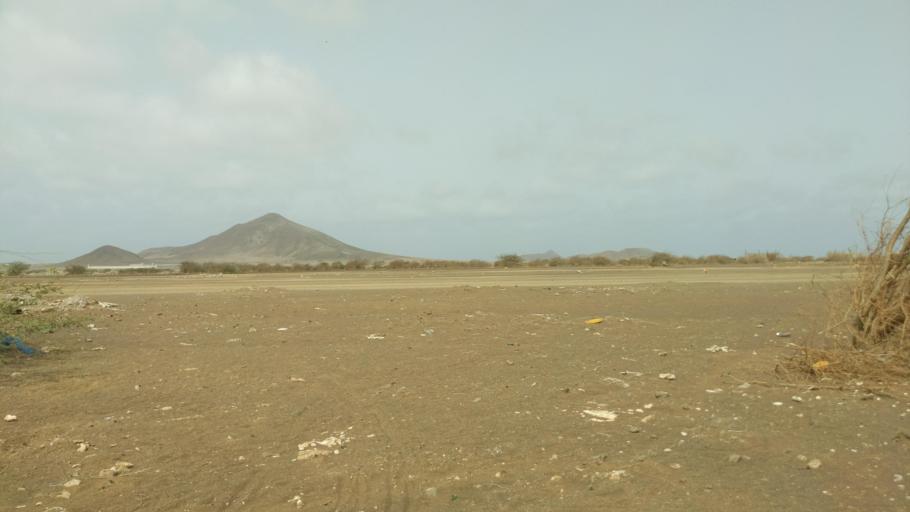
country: CV
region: Sal
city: Espargos
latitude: 16.7691
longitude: -22.9456
